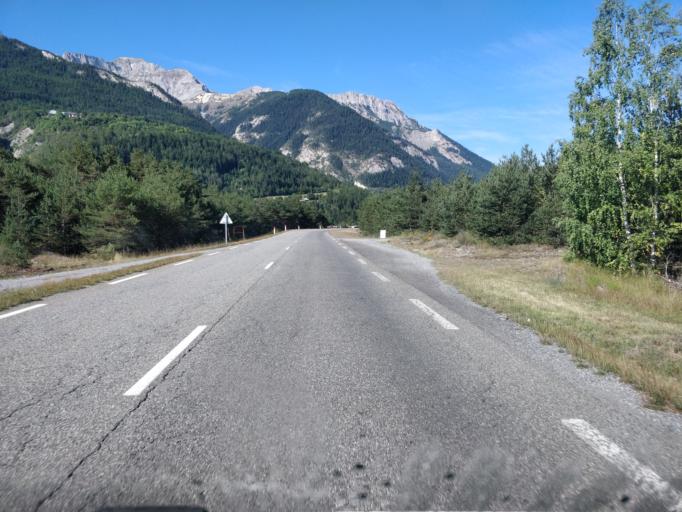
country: FR
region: Provence-Alpes-Cote d'Azur
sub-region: Departement des Alpes-de-Haute-Provence
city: Barcelonnette
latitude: 44.3905
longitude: 6.5874
